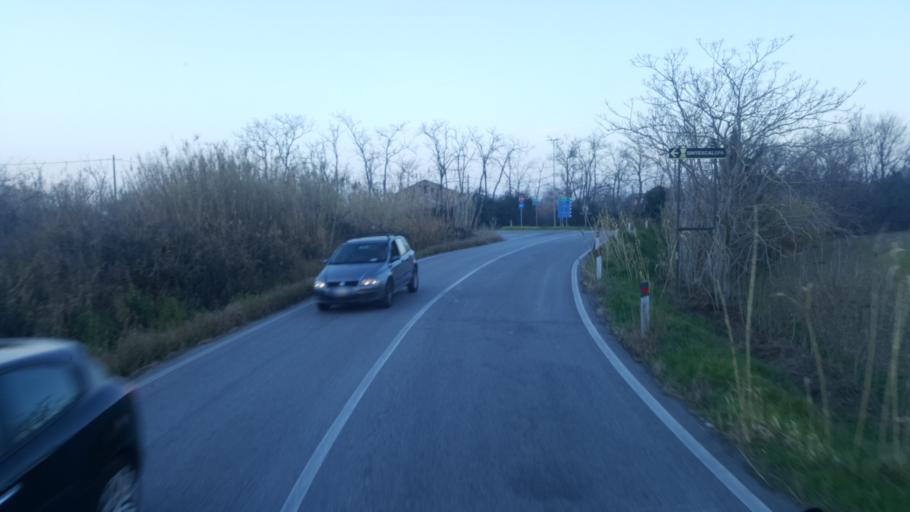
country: IT
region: The Marches
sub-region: Provincia di Ancona
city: Falconara Marittima
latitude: 43.6292
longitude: 13.3732
